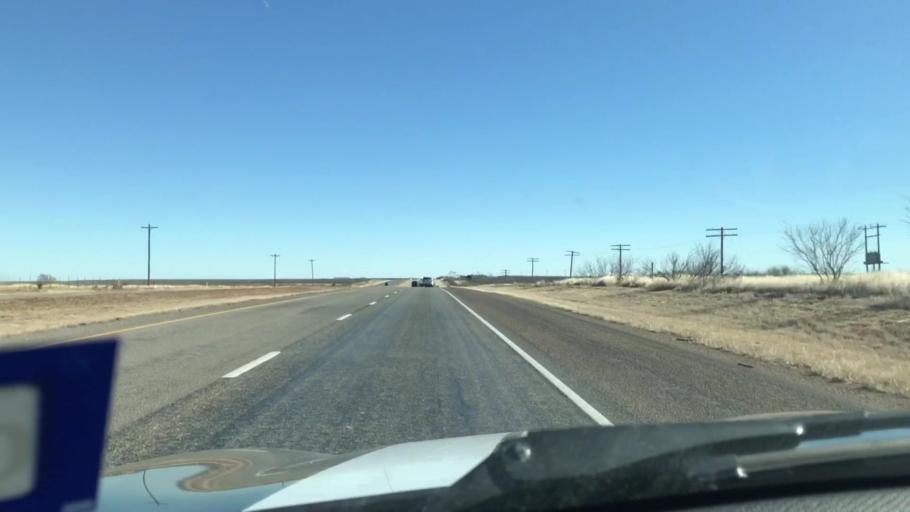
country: US
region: Texas
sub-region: Garza County
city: Post
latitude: 33.1343
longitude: -101.3068
